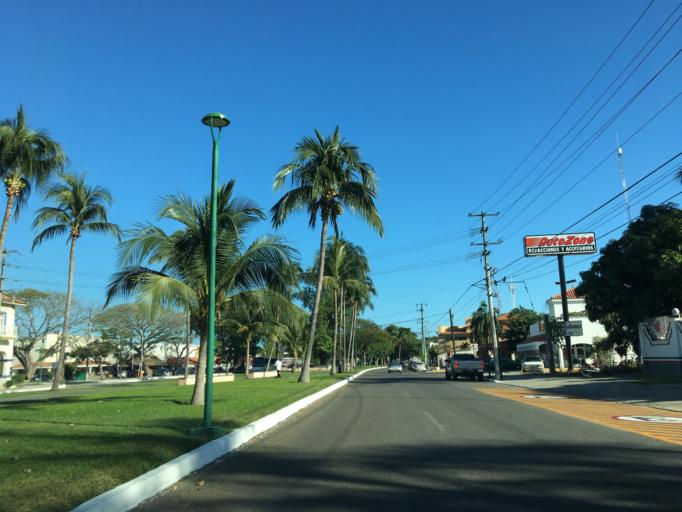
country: MX
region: Oaxaca
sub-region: Santa Maria Huatulco
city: Crucecita
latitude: 15.7632
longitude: -96.1316
